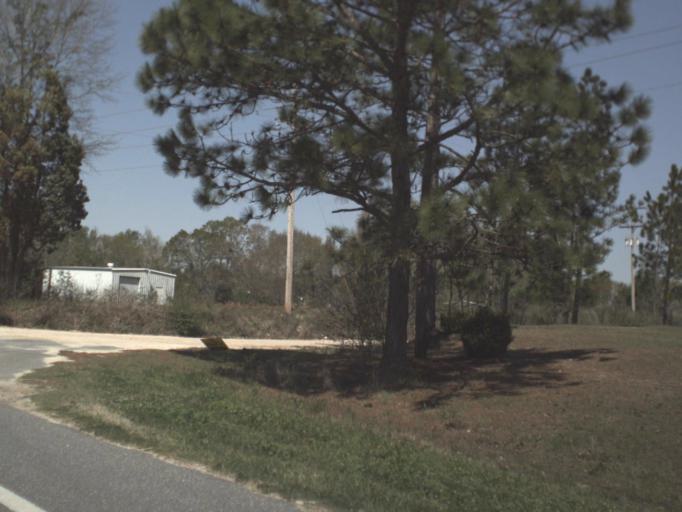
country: US
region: Florida
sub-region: Jackson County
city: Graceville
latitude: 30.9635
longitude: -85.5638
